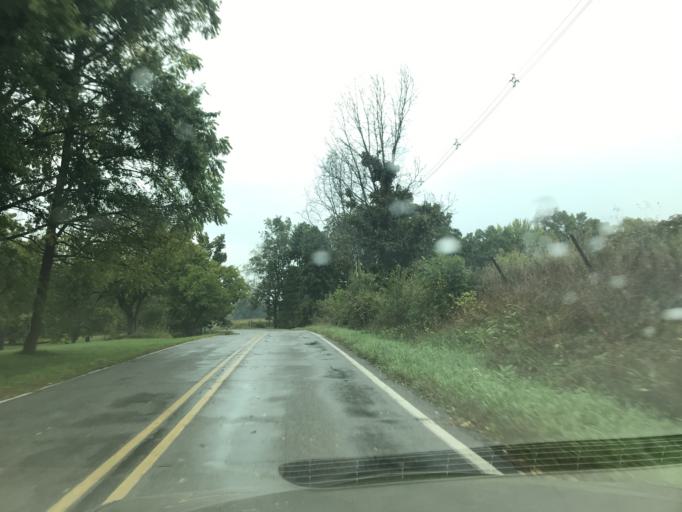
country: US
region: Michigan
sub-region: Ingham County
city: Leslie
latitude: 42.3671
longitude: -84.5459
